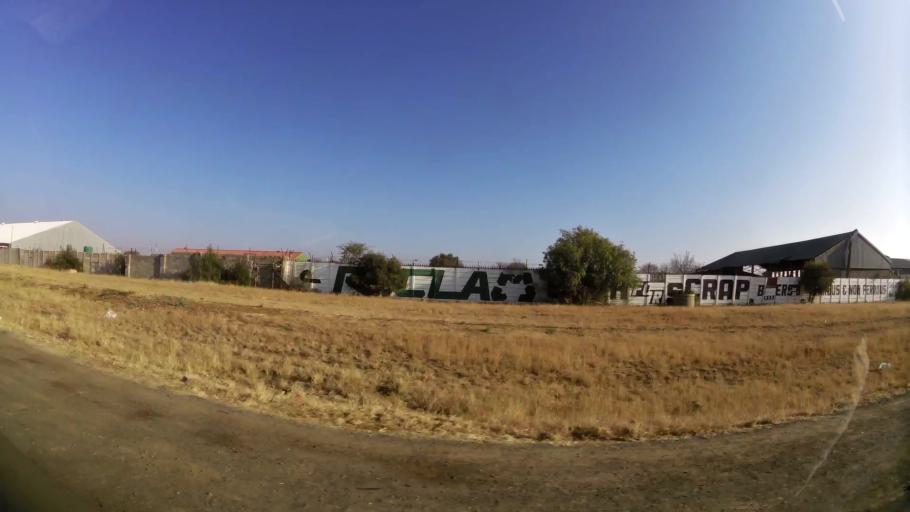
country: ZA
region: Orange Free State
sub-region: Mangaung Metropolitan Municipality
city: Bloemfontein
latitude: -29.1712
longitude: 26.2296
